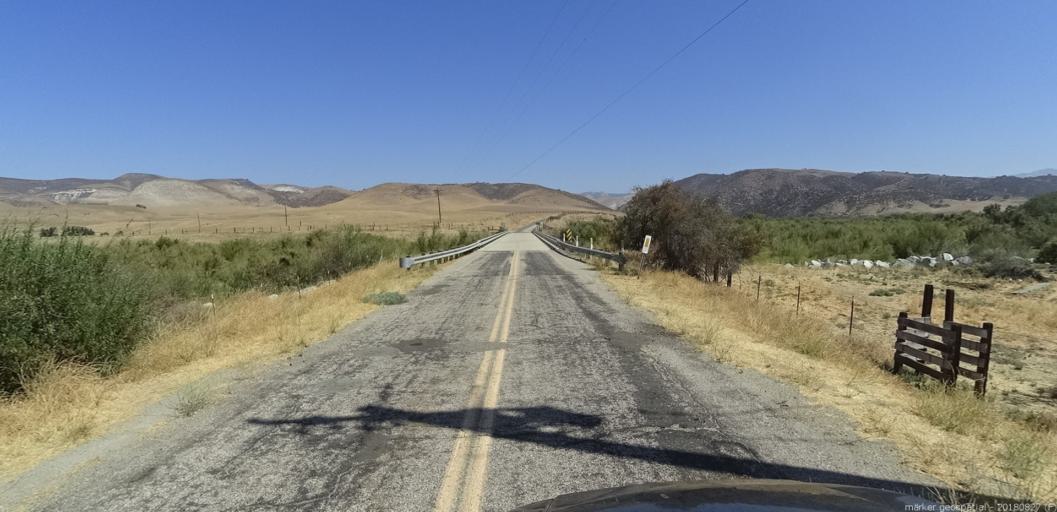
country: US
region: California
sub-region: Monterey County
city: King City
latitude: 36.2691
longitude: -120.9945
